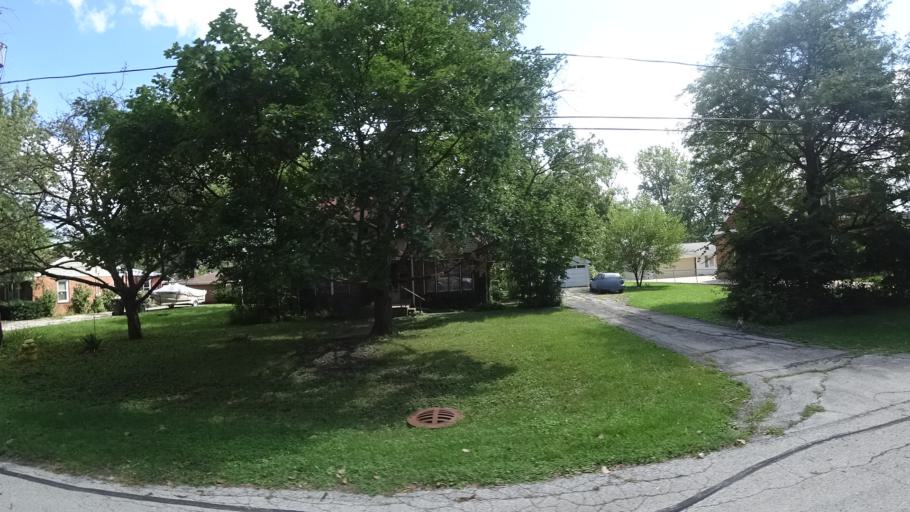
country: US
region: Illinois
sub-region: Cook County
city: Tinley Park
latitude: 41.5668
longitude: -87.7817
